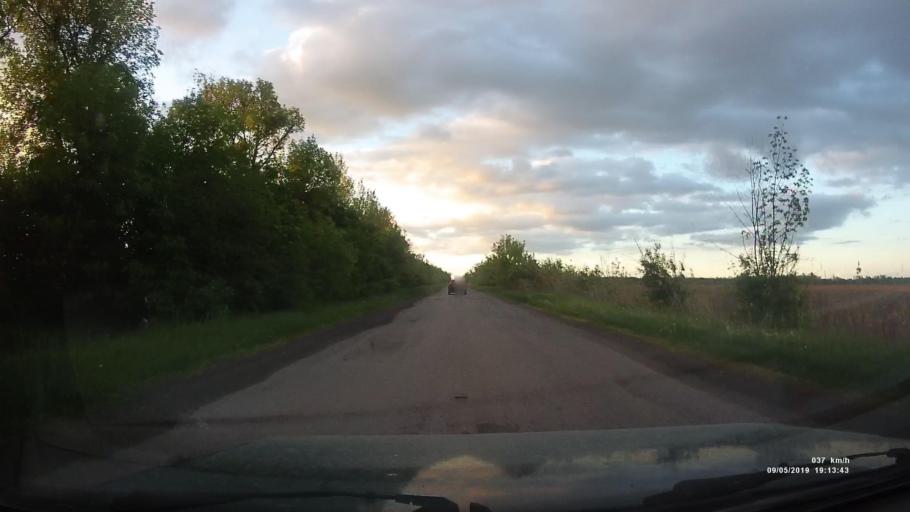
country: RU
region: Krasnodarskiy
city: Kanelovskaya
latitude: 46.7524
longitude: 39.2138
